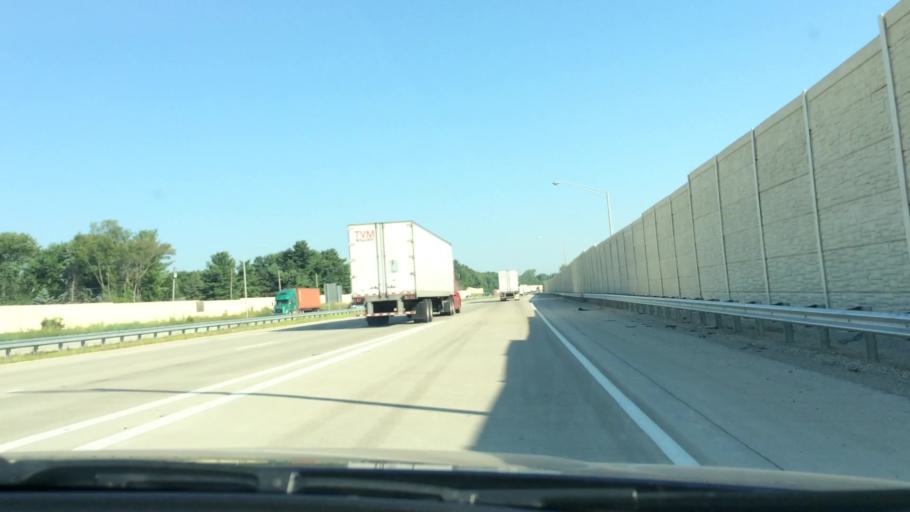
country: US
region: Indiana
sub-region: Tippecanoe County
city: Lafayette
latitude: 40.4209
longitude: -86.8236
